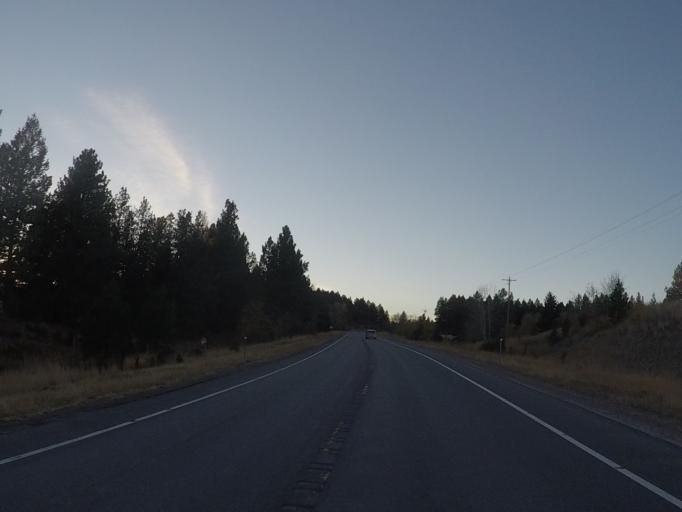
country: US
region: Montana
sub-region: Lewis and Clark County
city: Lincoln
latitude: 47.0078
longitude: -113.0525
